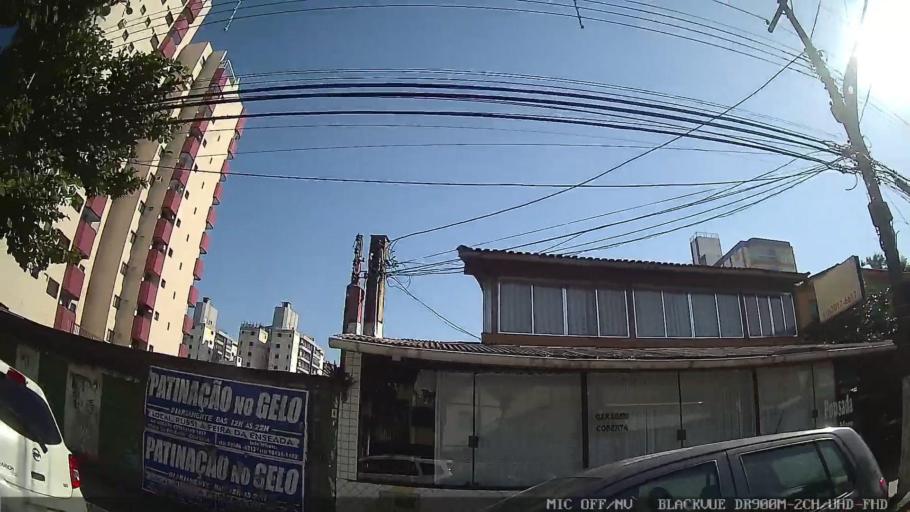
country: BR
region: Sao Paulo
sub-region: Guaruja
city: Guaruja
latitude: -24.0136
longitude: -46.2746
